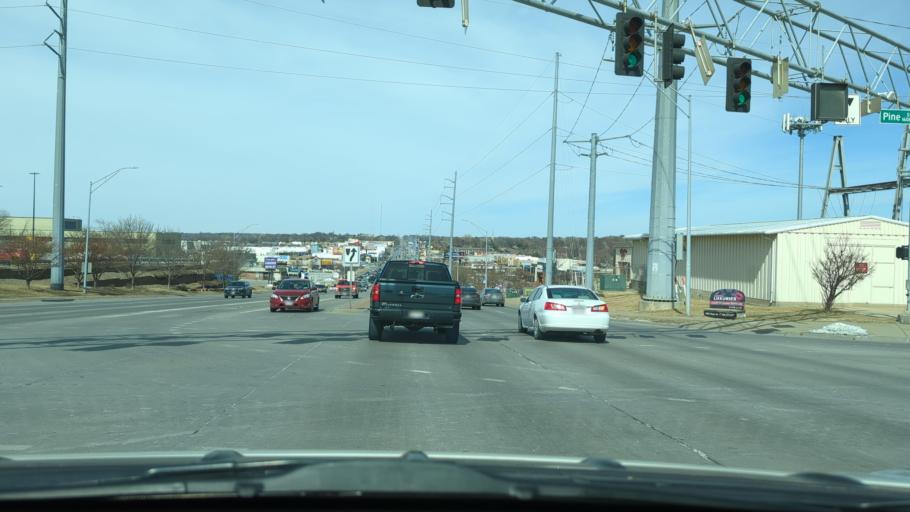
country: US
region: Nebraska
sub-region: Douglas County
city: Ralston
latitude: 41.2444
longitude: -96.0240
